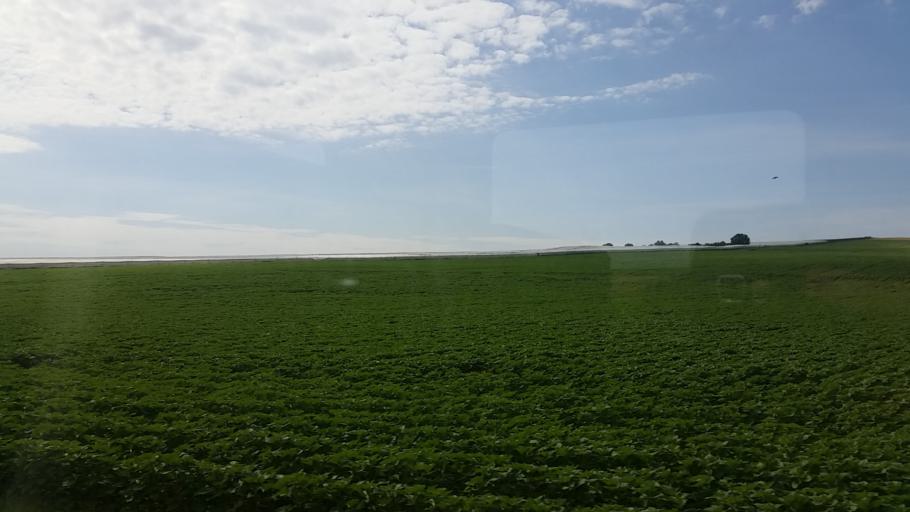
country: TR
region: Tekirdag
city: Marmaracik
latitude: 41.1638
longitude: 27.7092
